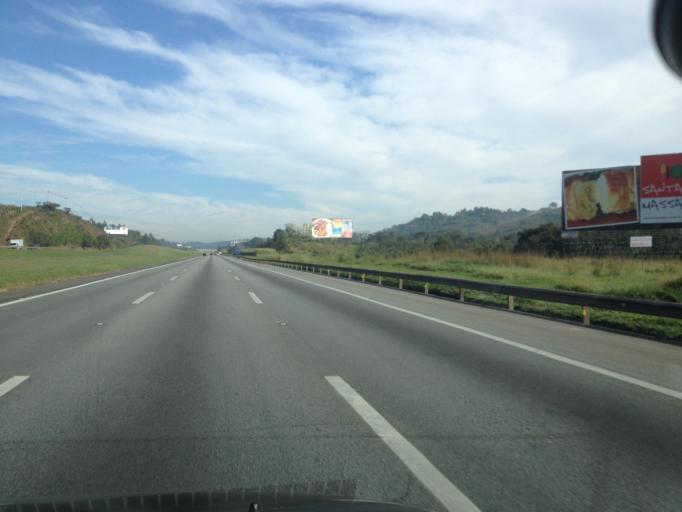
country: BR
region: Sao Paulo
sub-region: Sao Roque
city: Sao Roque
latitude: -23.4206
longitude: -47.1829
